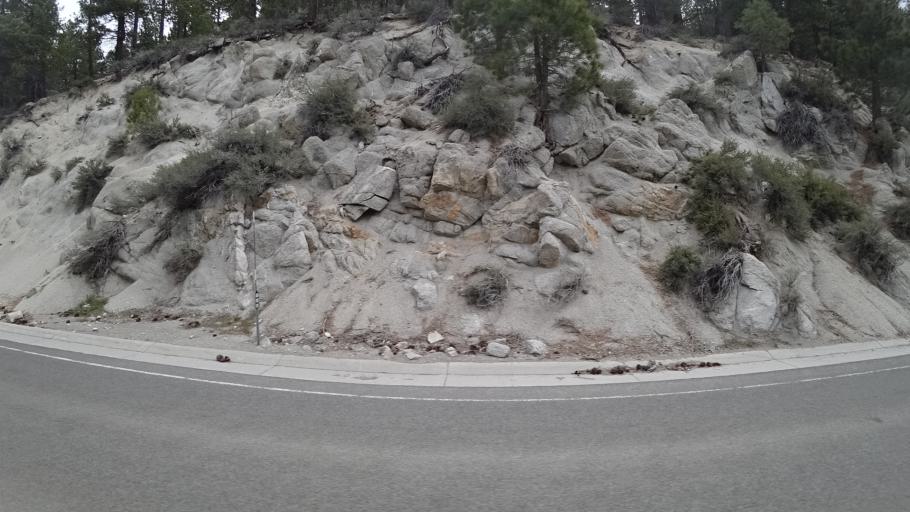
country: US
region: Nevada
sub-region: Washoe County
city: Incline Village
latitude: 39.1293
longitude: -119.9317
